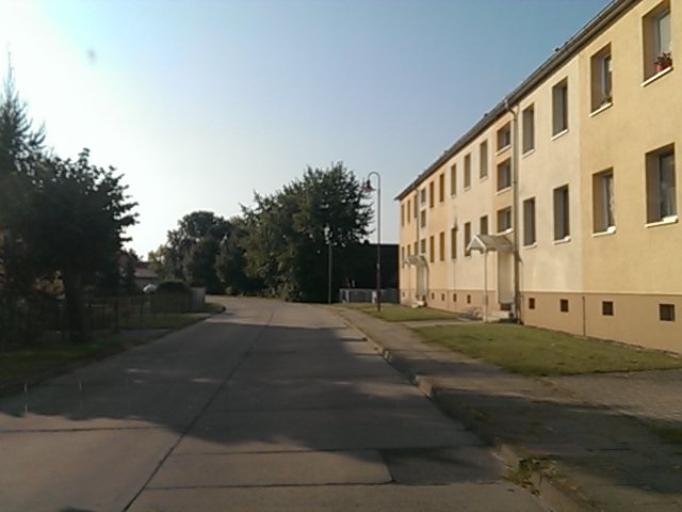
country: DE
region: Brandenburg
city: Michendorf
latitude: 52.2717
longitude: 13.1171
